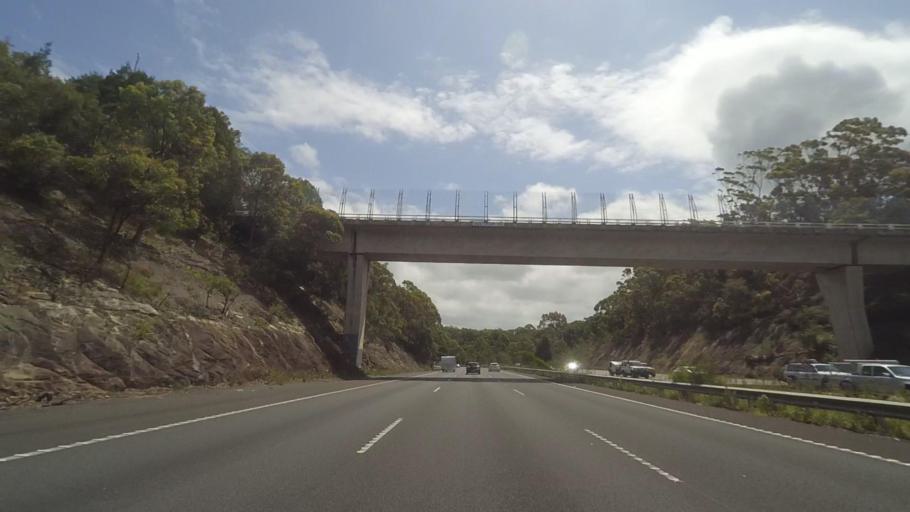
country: AU
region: New South Wales
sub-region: Gosford Shire
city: Lisarow
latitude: -33.3594
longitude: 151.3400
